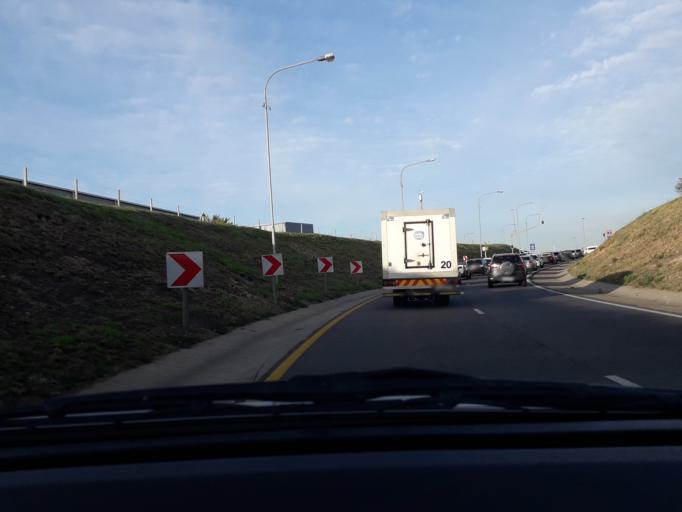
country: ZA
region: Gauteng
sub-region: City of Johannesburg Metropolitan Municipality
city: Midrand
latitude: -25.9317
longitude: 28.1456
